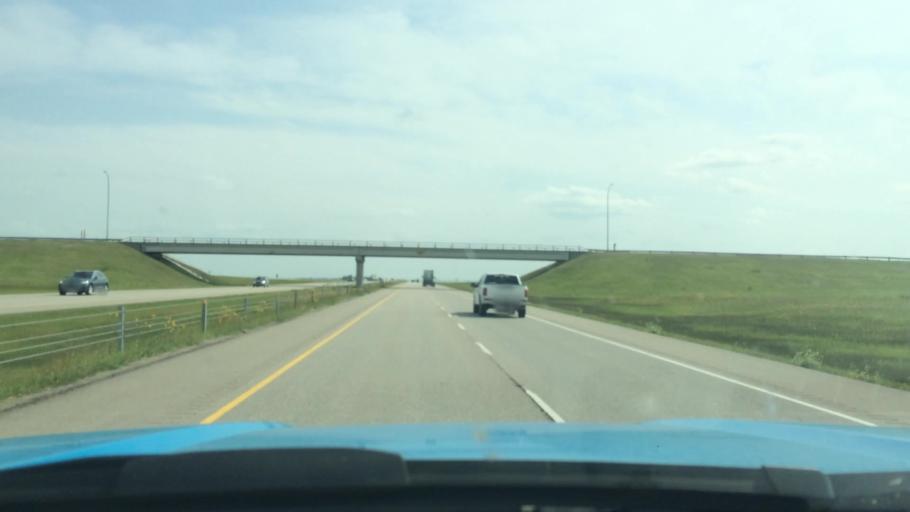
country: CA
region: Alberta
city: Didsbury
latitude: 51.6653
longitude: -114.0256
